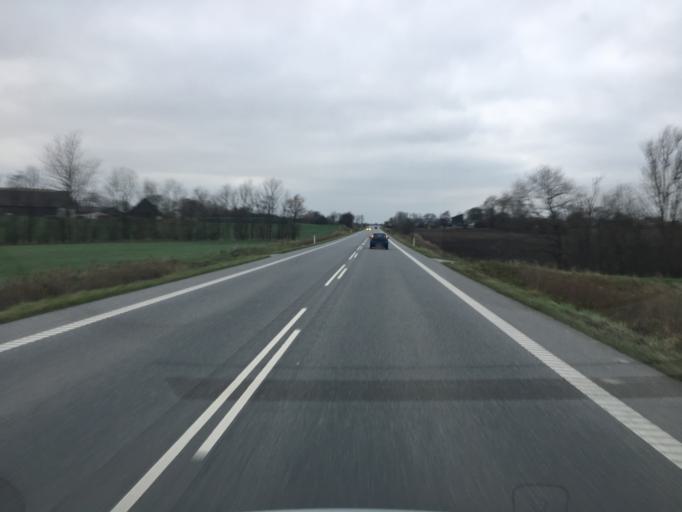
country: DK
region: South Denmark
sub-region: Aabenraa Kommune
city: Rodekro
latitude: 55.0259
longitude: 9.3538
